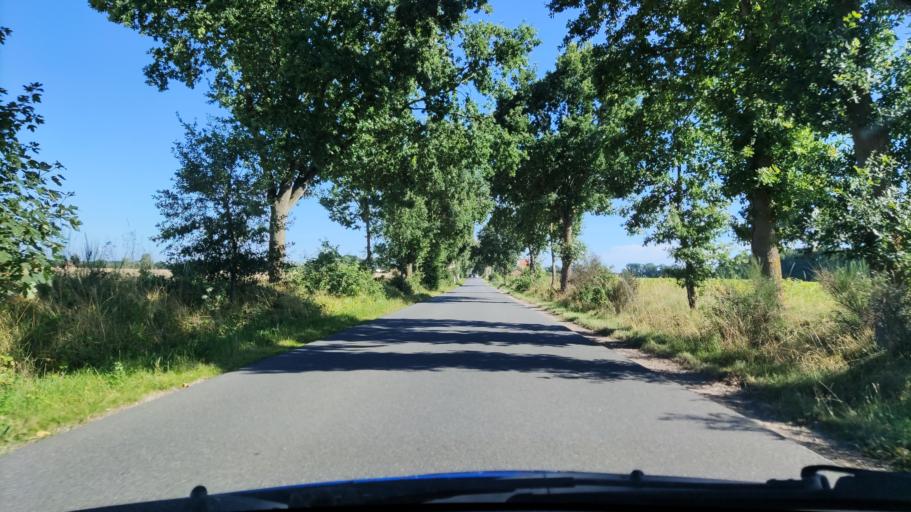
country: DE
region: Lower Saxony
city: Dahlenburg
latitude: 53.1757
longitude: 10.6991
